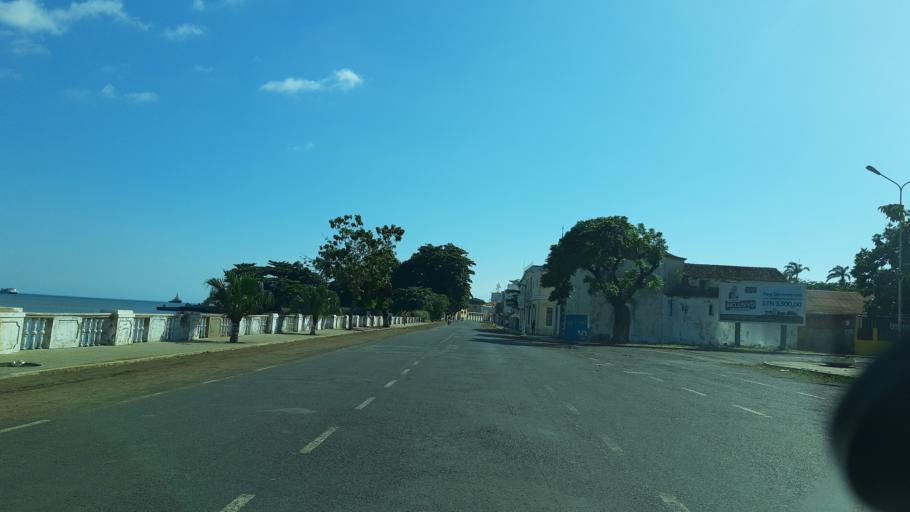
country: ST
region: Sao Tome Island
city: Sao Tome
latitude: 0.3411
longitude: 6.7351
